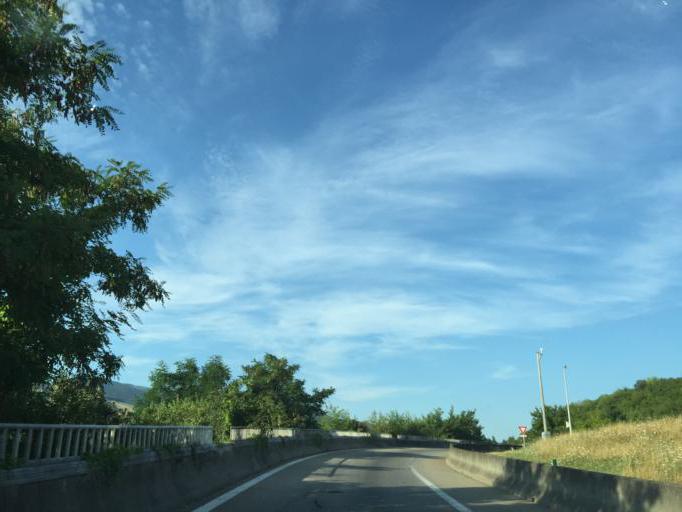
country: FR
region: Rhone-Alpes
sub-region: Departement de la Loire
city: Saint-Chamond
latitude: 45.4688
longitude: 4.4998
